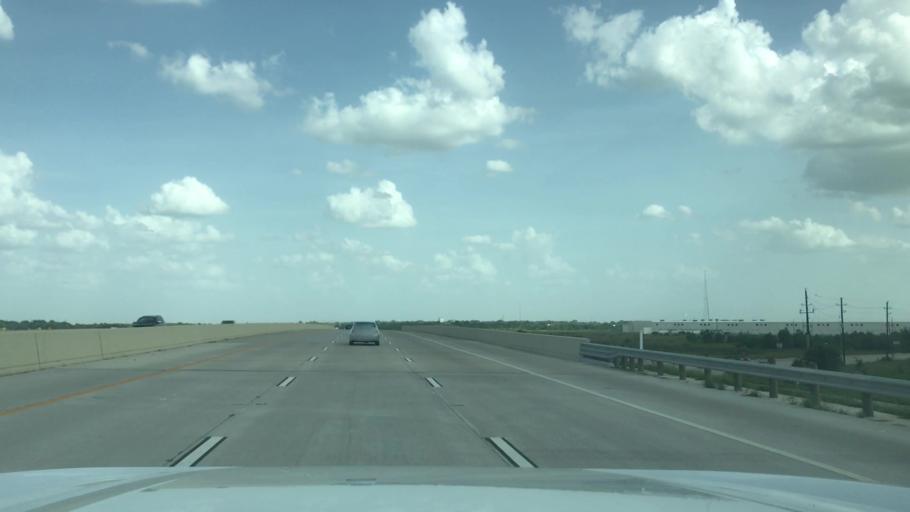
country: US
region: Texas
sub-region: Waller County
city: Waller
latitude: 30.0482
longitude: -95.8752
